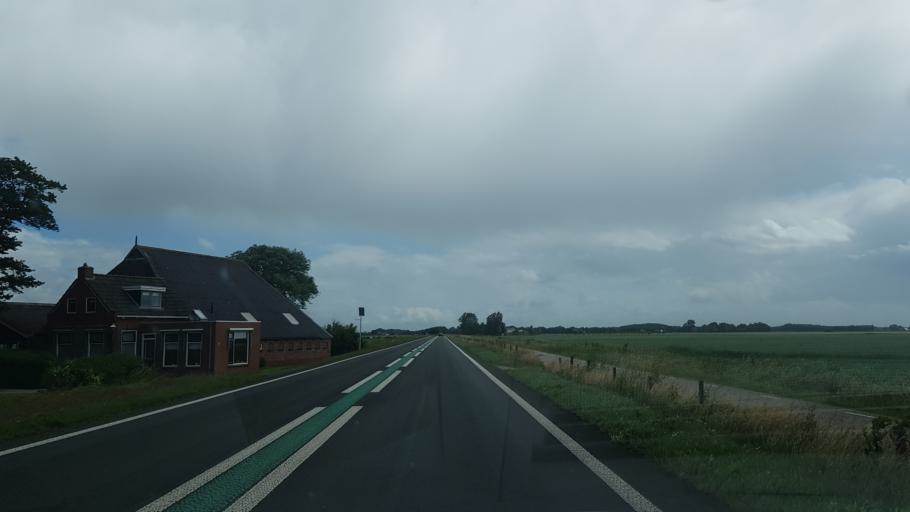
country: NL
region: Friesland
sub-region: Gemeente Dantumadiel
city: Rinsumageast
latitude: 53.2872
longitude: 5.9183
